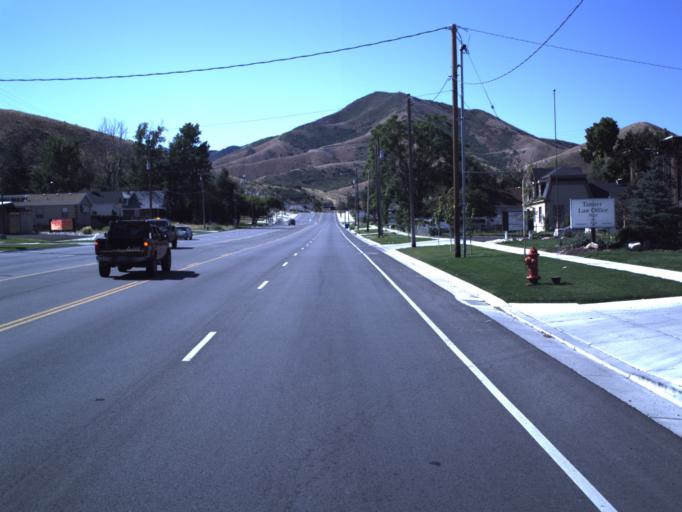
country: US
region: Utah
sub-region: Tooele County
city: Tooele
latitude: 40.5263
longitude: -112.2987
